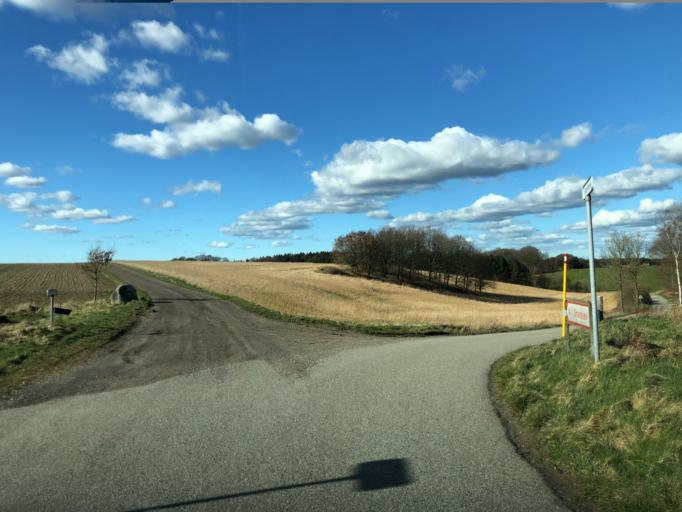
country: DK
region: Central Jutland
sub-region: Favrskov Kommune
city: Hammel
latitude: 56.3030
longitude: 9.9179
